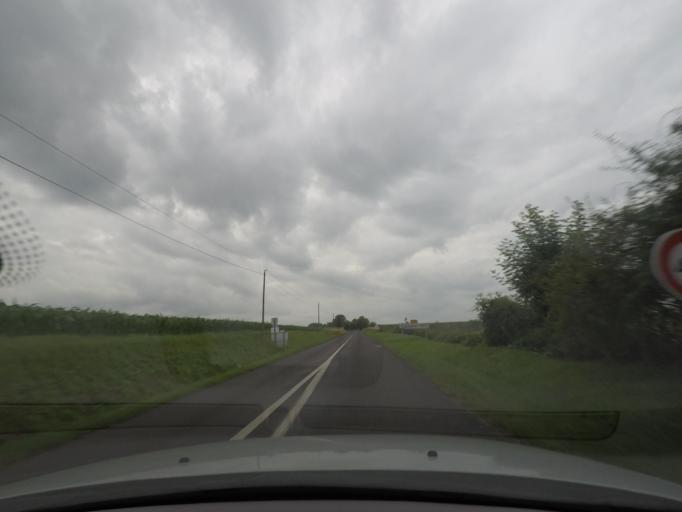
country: FR
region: Haute-Normandie
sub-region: Departement de la Seine-Maritime
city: Neufchatel-en-Bray
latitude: 49.7315
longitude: 1.4550
